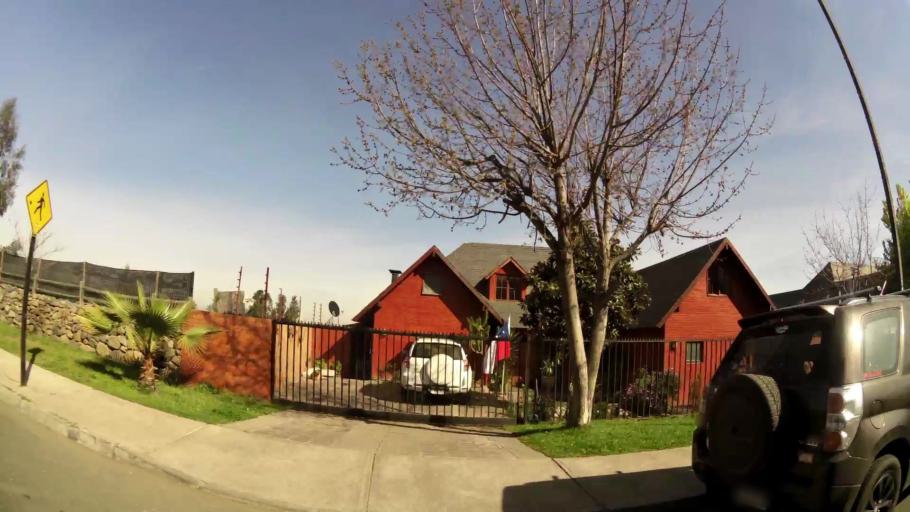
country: CL
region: Santiago Metropolitan
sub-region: Provincia de Santiago
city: Villa Presidente Frei, Nunoa, Santiago, Chile
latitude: -33.4999
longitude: -70.5270
